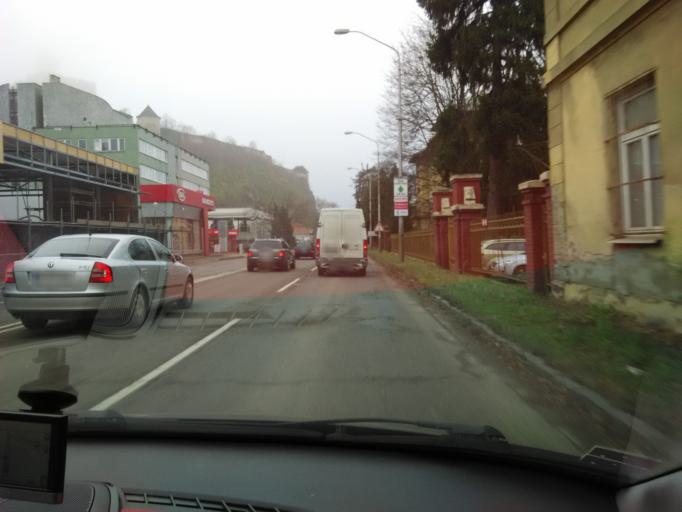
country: SK
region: Trenciansky
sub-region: Okres Trencin
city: Trencin
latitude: 48.8937
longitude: 18.0508
